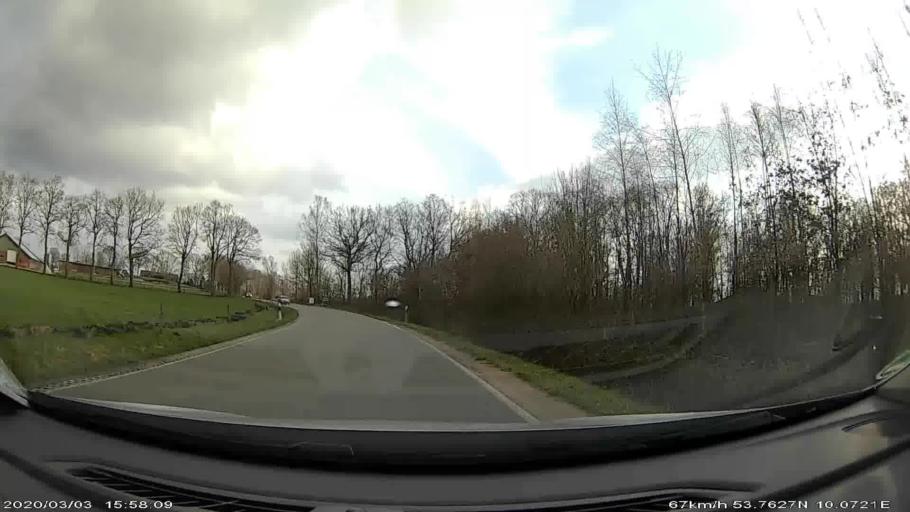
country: DE
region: Schleswig-Holstein
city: Tangstedt
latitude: 53.7640
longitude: 10.0715
